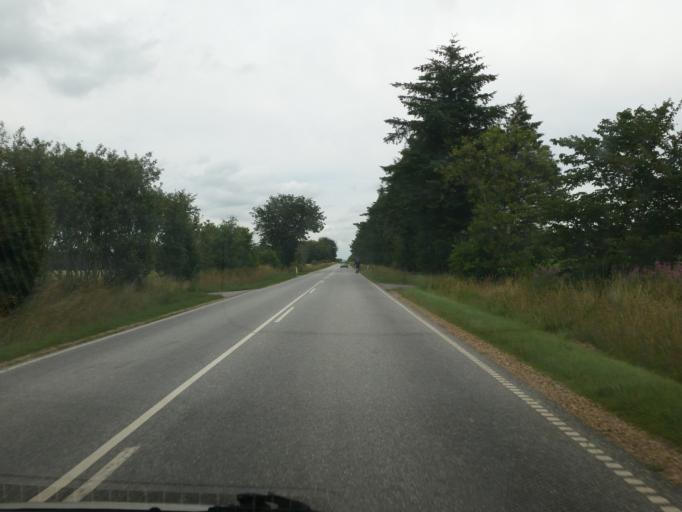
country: DK
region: South Denmark
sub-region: Esbjerg Kommune
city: Ribe
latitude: 55.3783
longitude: 8.8279
